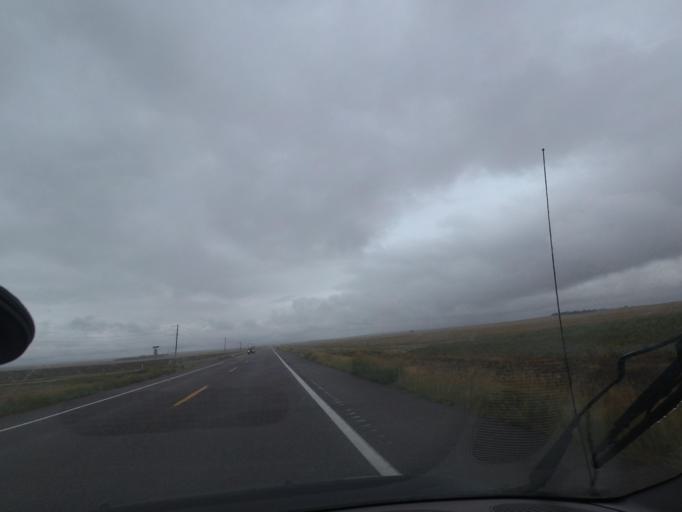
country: US
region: Colorado
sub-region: Arapahoe County
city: Byers
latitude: 39.7395
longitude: -104.1540
